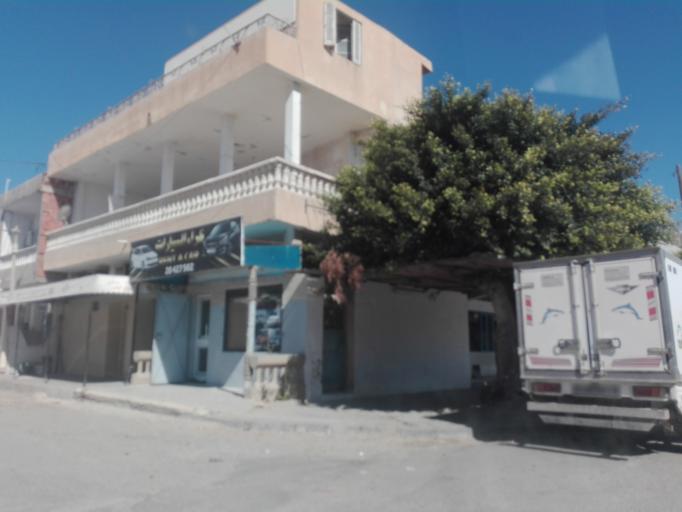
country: TN
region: Safaqis
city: Al Qarmadah
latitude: 34.7064
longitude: 11.2028
